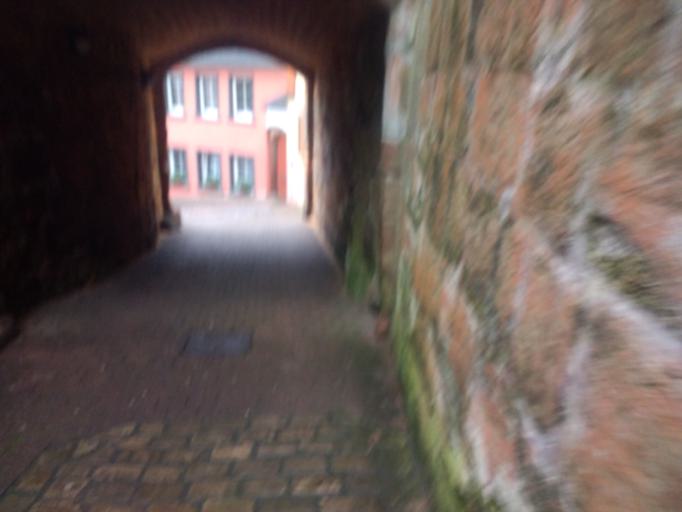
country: DE
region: Rheinland-Pfalz
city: Saarburg
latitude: 49.6075
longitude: 6.5514
